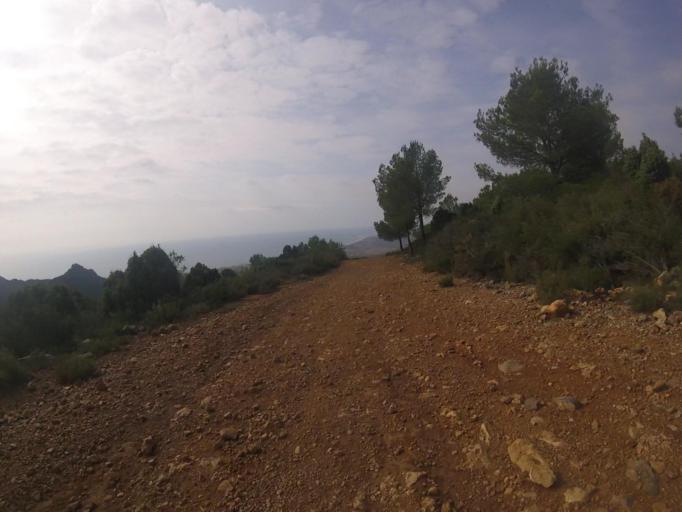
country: ES
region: Valencia
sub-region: Provincia de Castello
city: Benicassim
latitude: 40.0855
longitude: 0.0402
